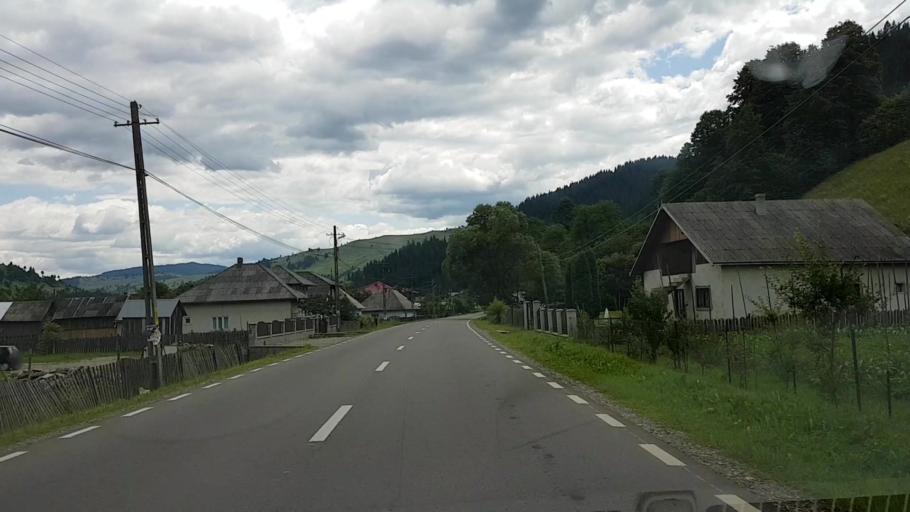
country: RO
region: Neamt
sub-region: Comuna Borca
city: Borca
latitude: 47.1891
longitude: 25.7728
